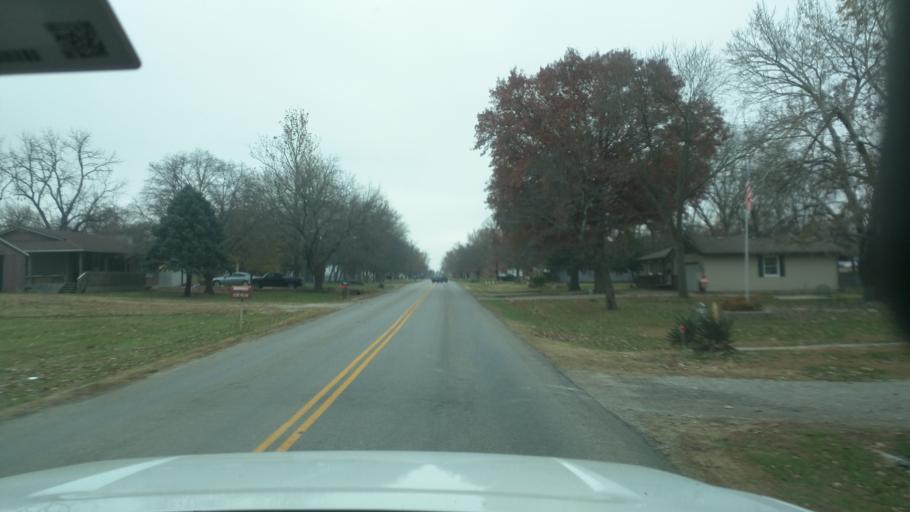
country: US
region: Kansas
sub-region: Lyon County
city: Emporia
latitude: 38.5132
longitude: -96.2619
